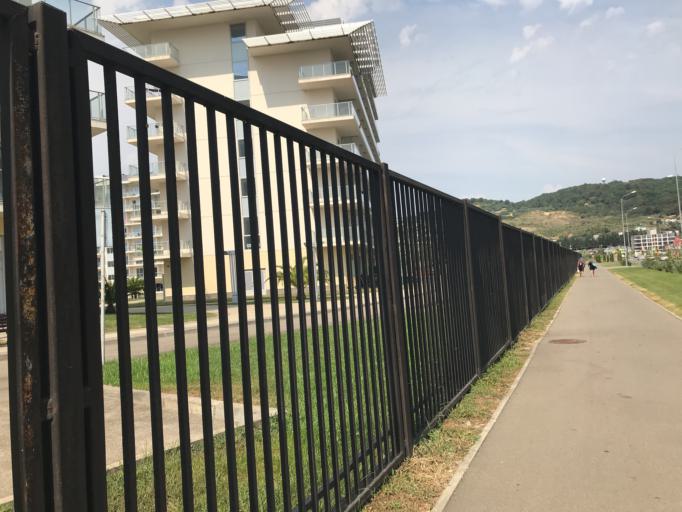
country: RU
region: Krasnodarskiy
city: Adler
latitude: 43.4024
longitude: 39.9785
